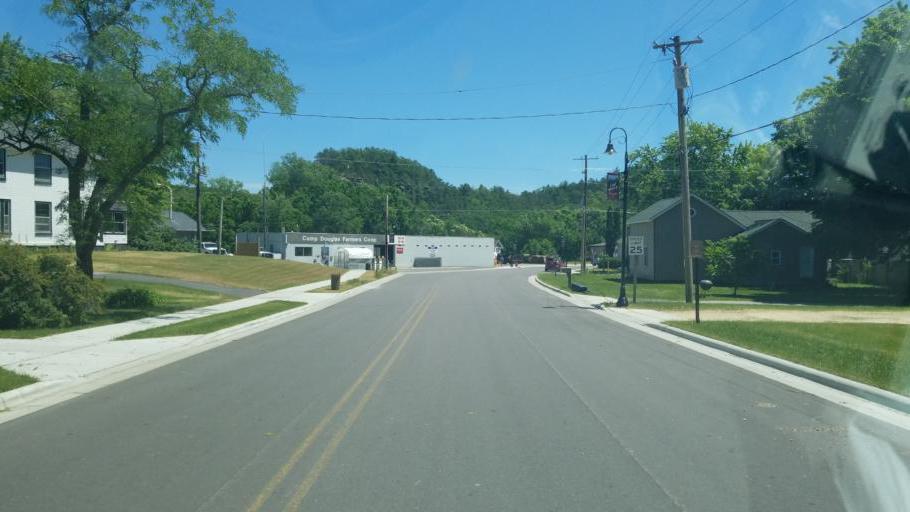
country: US
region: Wisconsin
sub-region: Juneau County
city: New Lisbon
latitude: 43.9205
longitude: -90.2702
